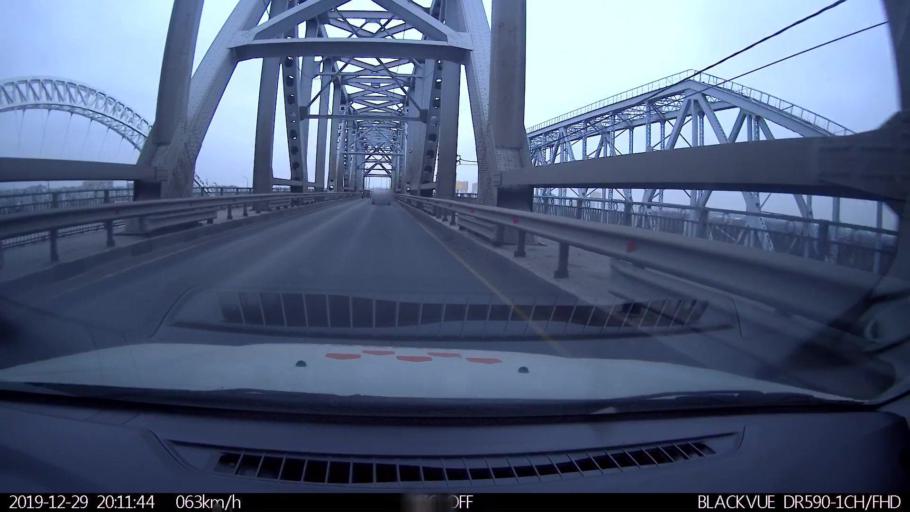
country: RU
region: Nizjnij Novgorod
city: Neklyudovo
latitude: 56.3540
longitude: 43.9247
